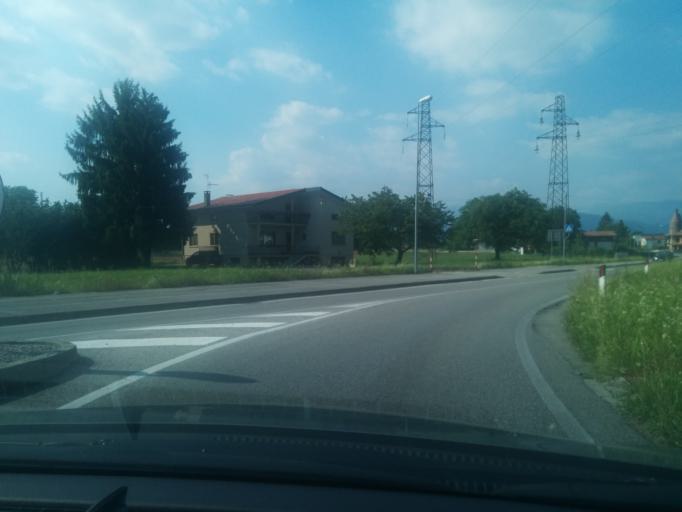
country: IT
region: Friuli Venezia Giulia
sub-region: Provincia di Udine
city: Reana del Rojale
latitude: 46.1409
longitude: 13.2432
